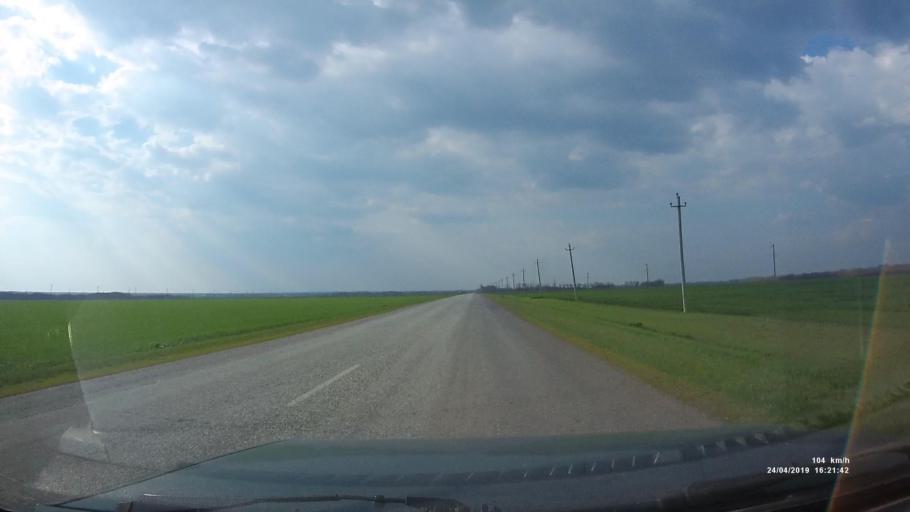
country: RU
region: Rostov
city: Orlovskiy
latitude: 46.8087
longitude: 42.0629
